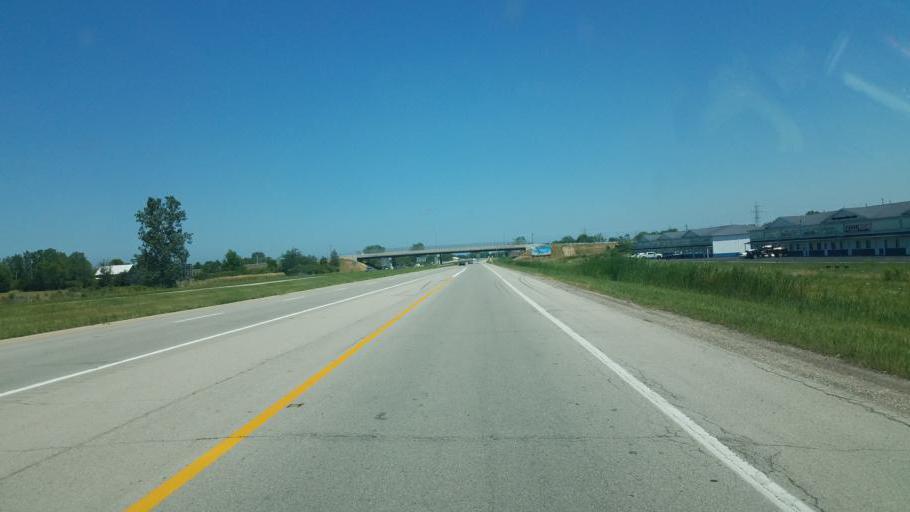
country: US
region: Ohio
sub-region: Ottawa County
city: Port Clinton
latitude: 41.5056
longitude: -82.8549
